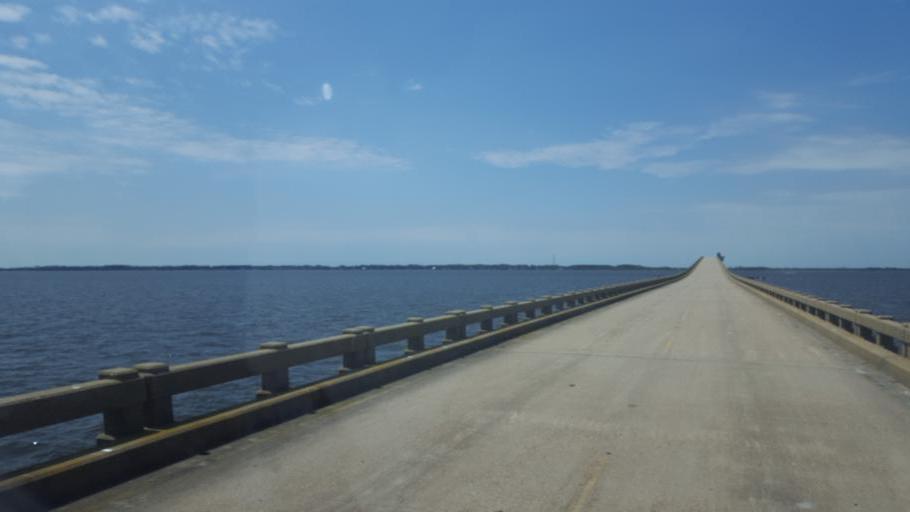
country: US
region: North Carolina
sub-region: Dare County
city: Manteo
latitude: 35.9207
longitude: -75.7429
